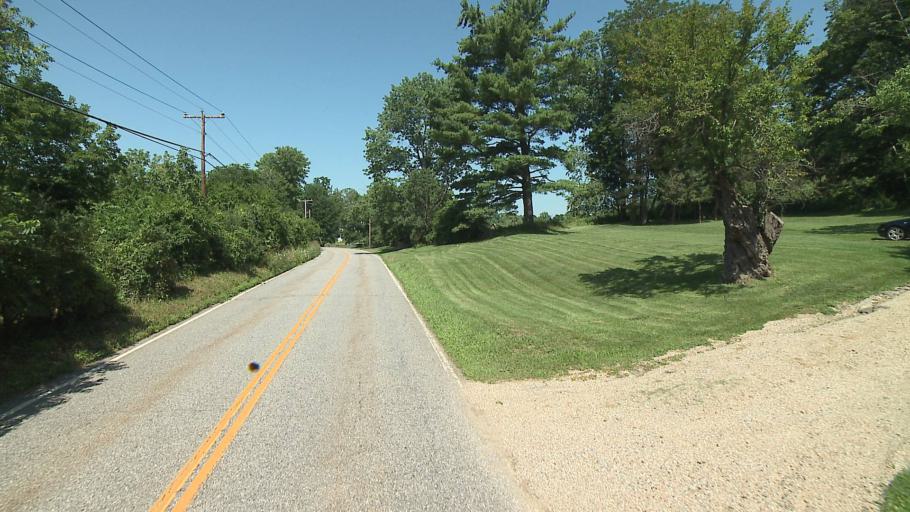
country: US
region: Connecticut
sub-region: Litchfield County
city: Kent
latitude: 41.8933
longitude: -73.4840
